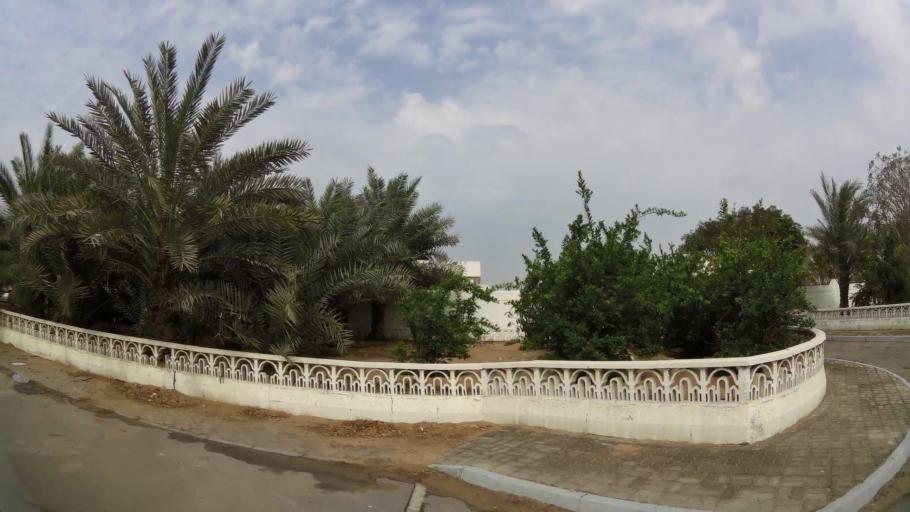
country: AE
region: Abu Dhabi
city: Abu Dhabi
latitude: 24.6489
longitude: 54.7344
